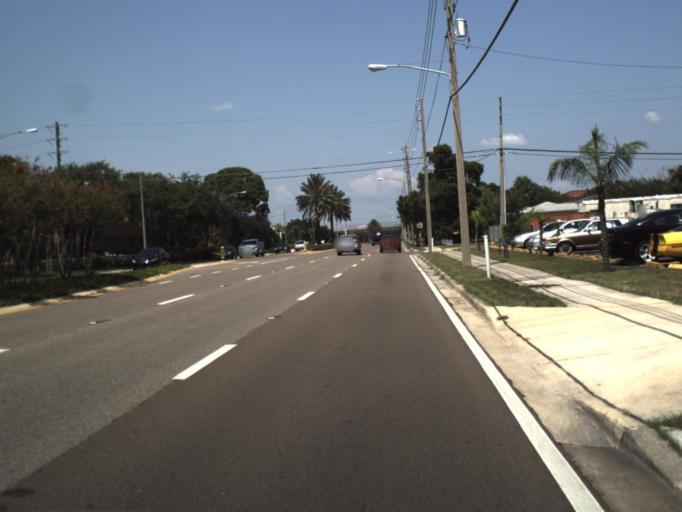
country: US
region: Florida
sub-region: Pinellas County
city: South Pasadena
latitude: 27.7640
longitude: -82.7343
